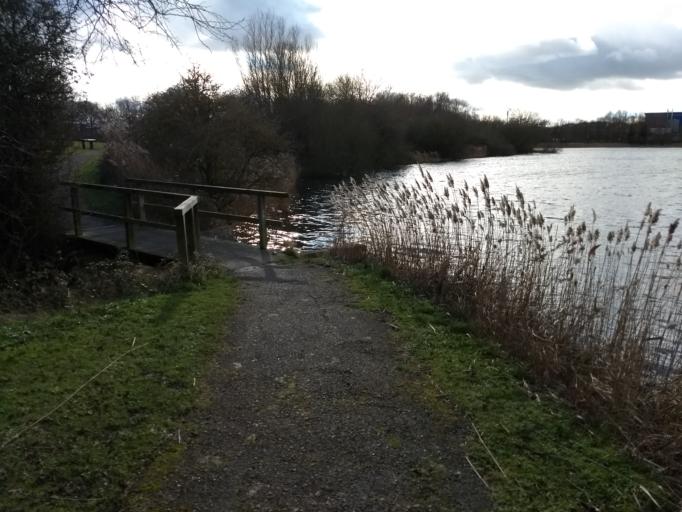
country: GB
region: England
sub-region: Buckinghamshire
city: Bletchley
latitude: 52.0063
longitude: -0.7222
